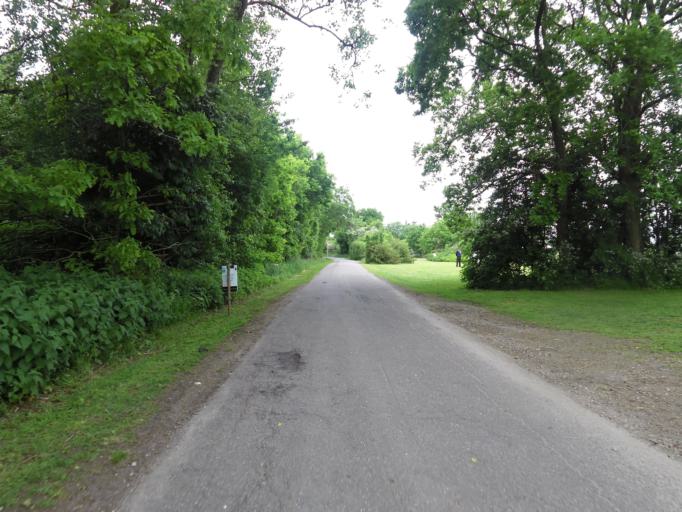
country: DK
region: South Denmark
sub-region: Esbjerg Kommune
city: Ribe
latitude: 55.3231
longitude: 8.8221
